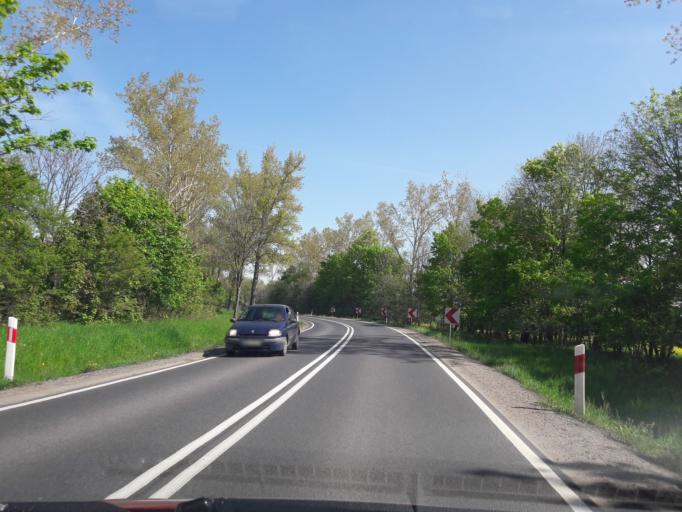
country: PL
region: Lower Silesian Voivodeship
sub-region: Powiat klodzki
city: Bystrzyca Klodzka
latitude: 50.2288
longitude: 16.6773
